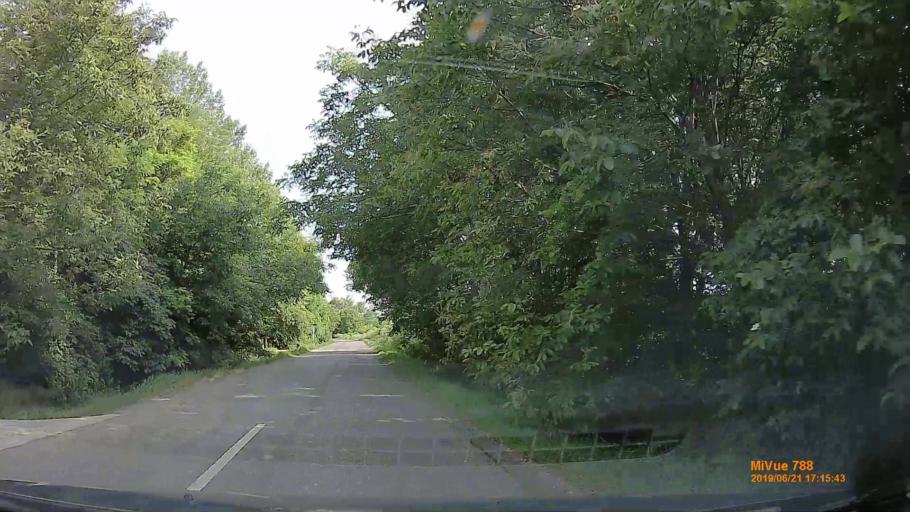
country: HU
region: Baranya
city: Pecsvarad
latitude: 46.1519
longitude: 18.4234
